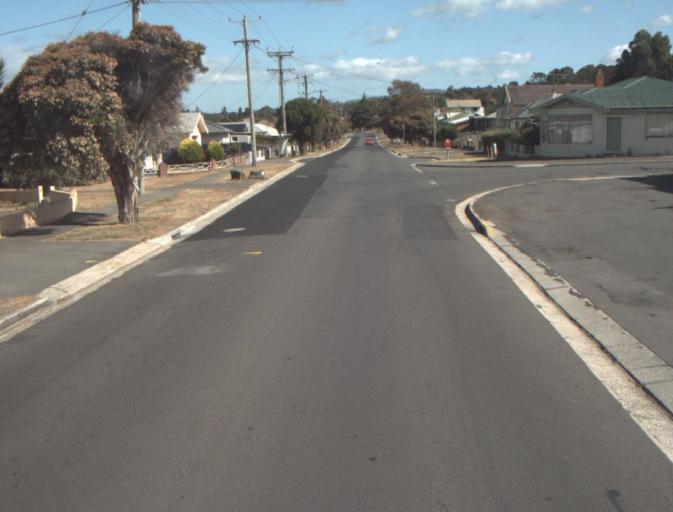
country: AU
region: Tasmania
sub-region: Launceston
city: Newstead
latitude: -41.4258
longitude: 147.1743
